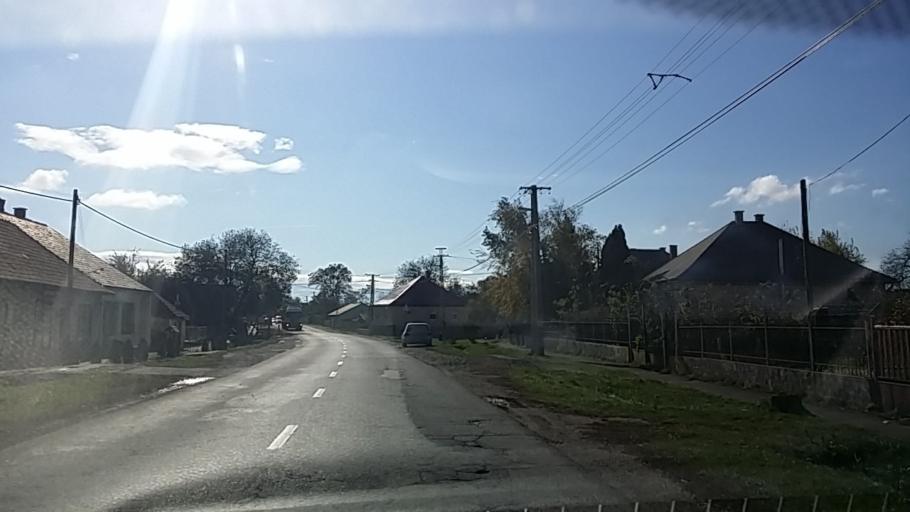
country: HU
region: Borsod-Abauj-Zemplen
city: Gonc
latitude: 48.4157
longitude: 21.2310
